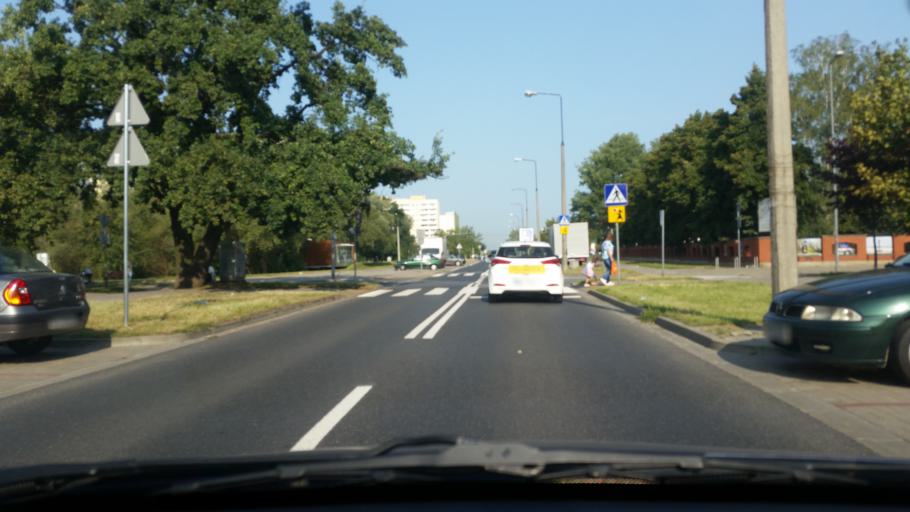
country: PL
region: Masovian Voivodeship
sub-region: Warszawa
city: Bialoleka
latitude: 52.3198
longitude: 20.9567
